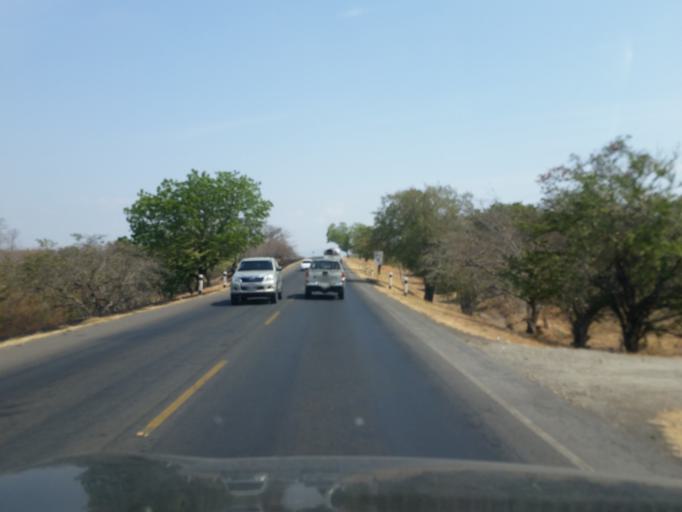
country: NI
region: Managua
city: Tipitapa
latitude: 12.3289
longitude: -86.0522
